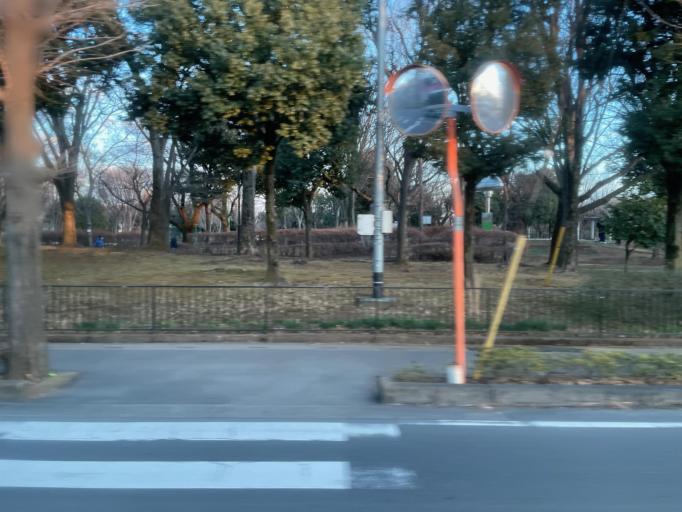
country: JP
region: Saitama
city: Asaka
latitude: 35.7960
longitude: 139.5901
